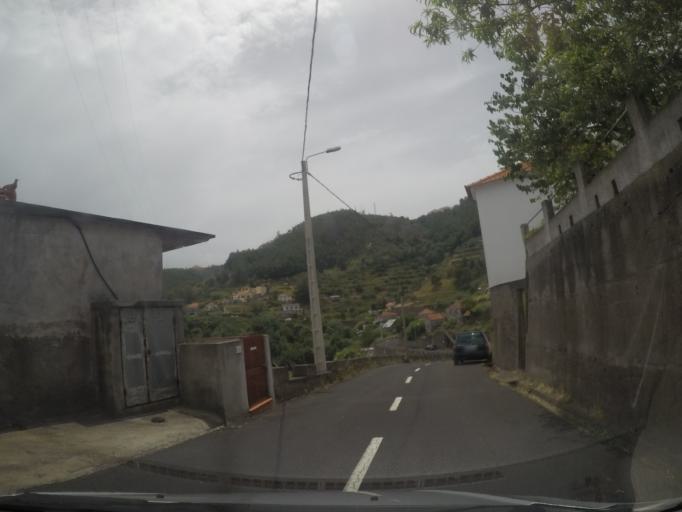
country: PT
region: Madeira
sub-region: Santa Cruz
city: Camacha
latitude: 32.6728
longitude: -16.8392
